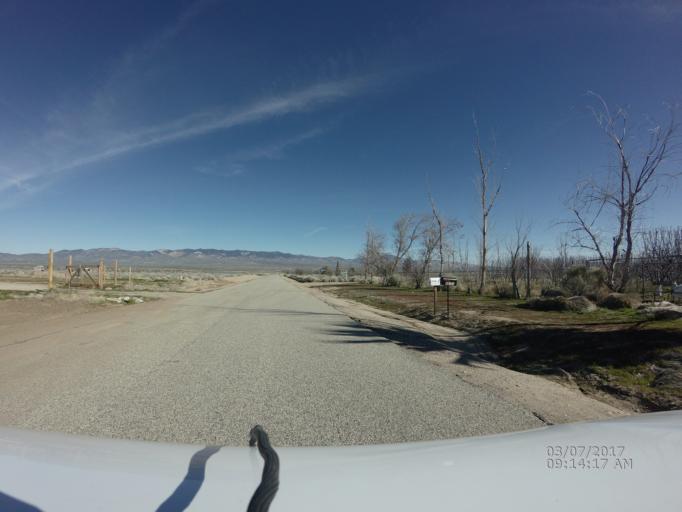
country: US
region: California
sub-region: Los Angeles County
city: Green Valley
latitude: 34.7851
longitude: -118.5900
